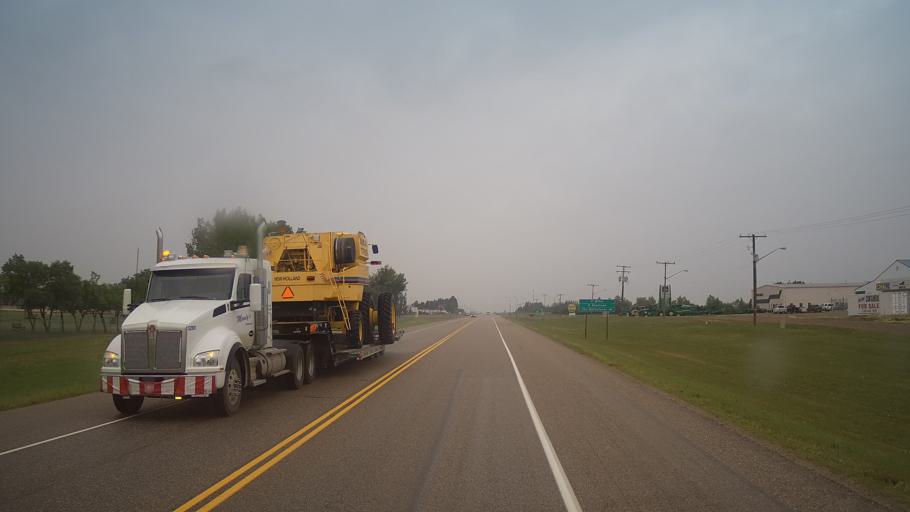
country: CA
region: Saskatchewan
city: Biggar
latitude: 52.0613
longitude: -107.9741
